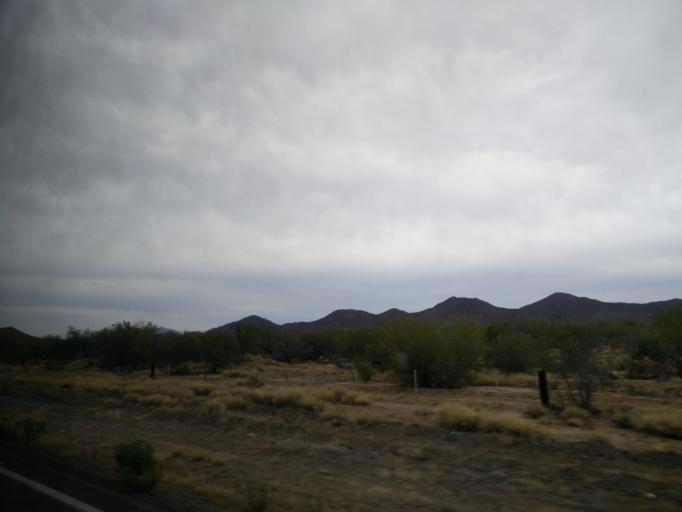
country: MX
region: Sonora
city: Hermosillo
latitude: 28.7799
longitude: -110.9644
